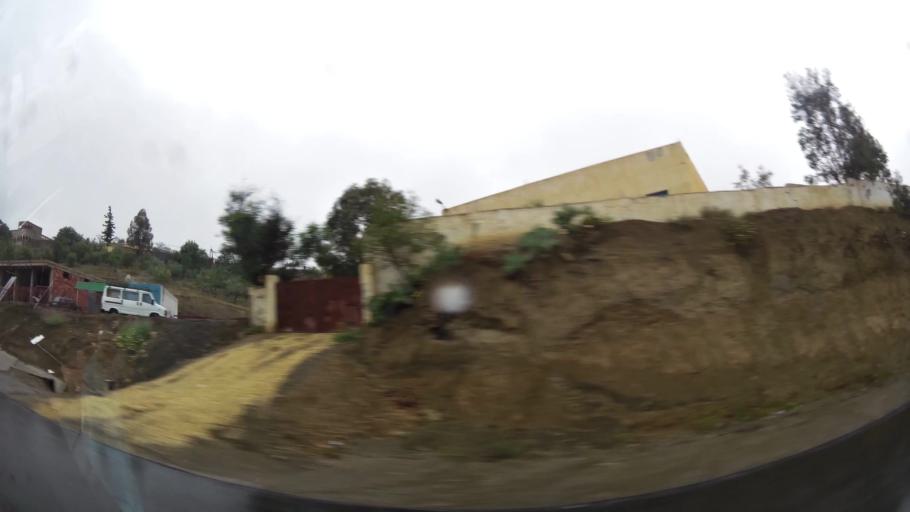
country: MA
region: Oriental
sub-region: Nador
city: Midar
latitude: 34.8293
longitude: -3.7196
